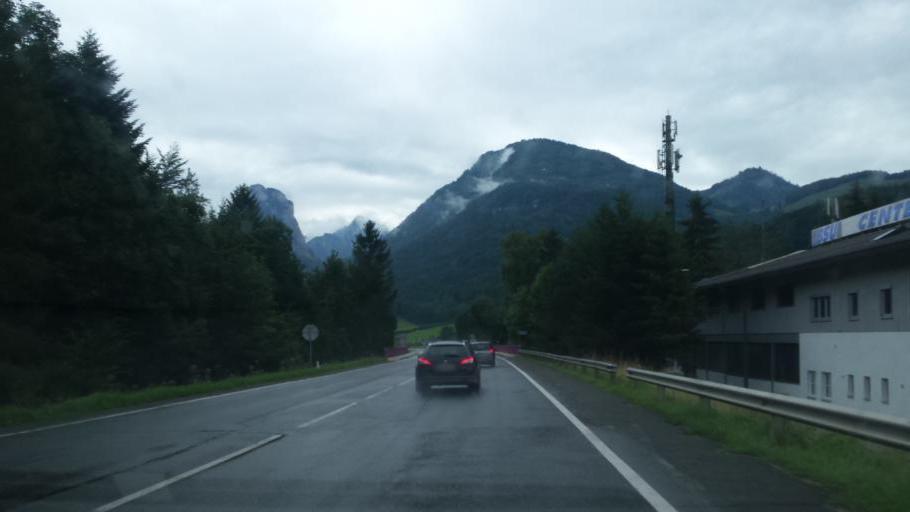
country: AT
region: Upper Austria
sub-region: Politischer Bezirk Gmunden
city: Sankt Wolfgang im Salzkammergut
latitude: 47.7274
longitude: 13.4203
